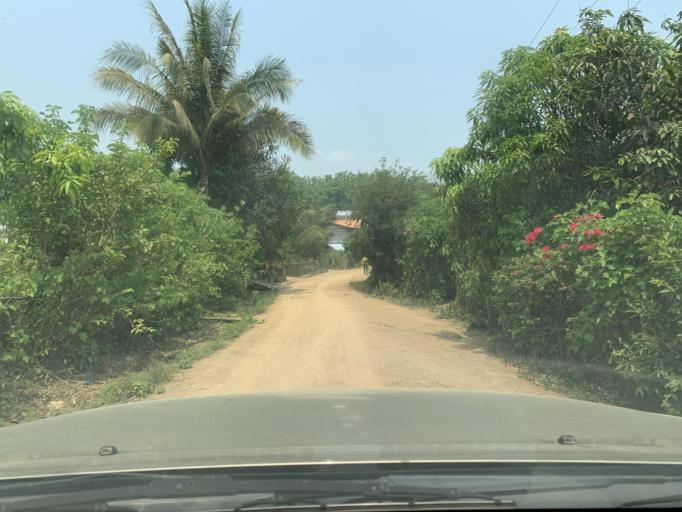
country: LA
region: Louangphabang
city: Louangphabang
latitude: 19.9462
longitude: 102.1341
